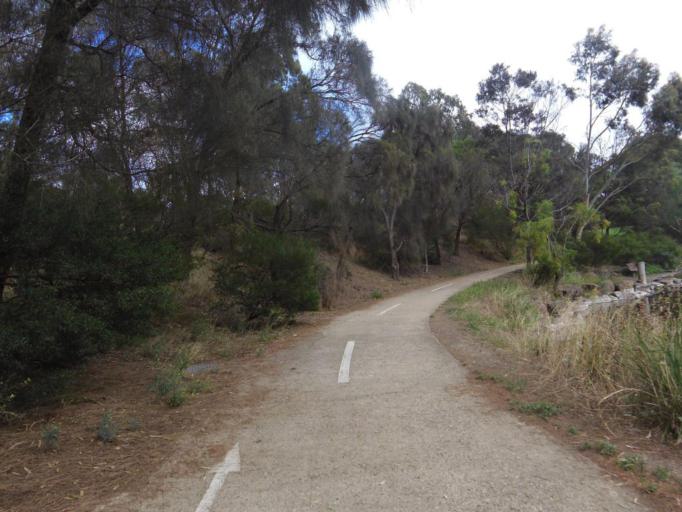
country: AU
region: Victoria
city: Alphington
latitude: -37.7737
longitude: 145.0336
